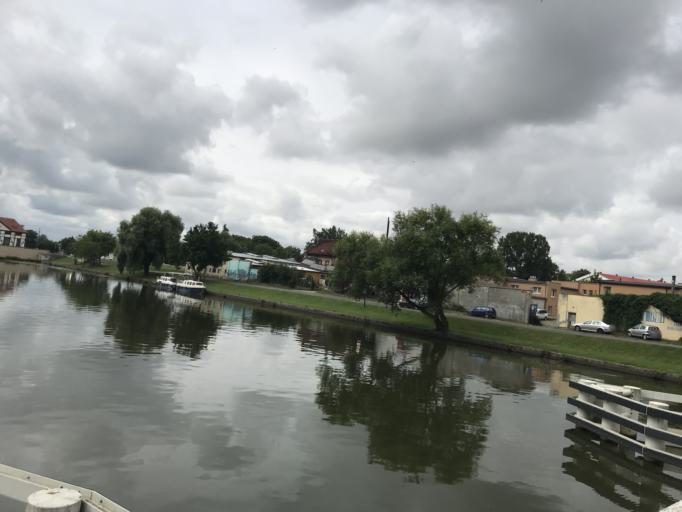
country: PL
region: Warmian-Masurian Voivodeship
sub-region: Powiat elblaski
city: Elblag
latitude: 54.1599
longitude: 19.3916
